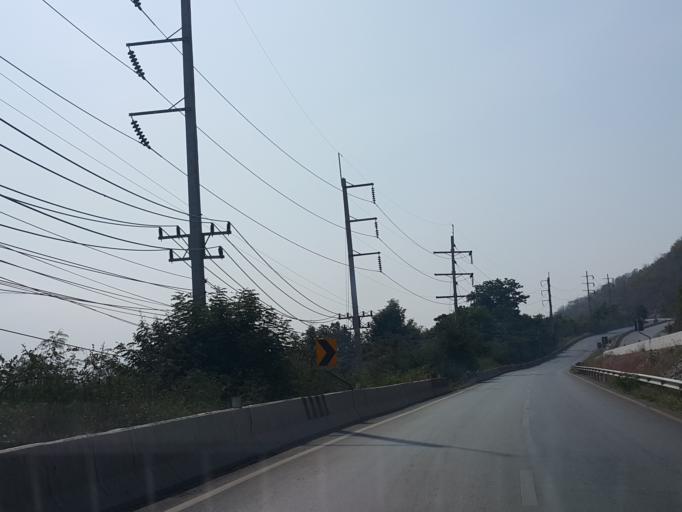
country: TH
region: Chiang Mai
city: Chom Thong
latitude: 18.3814
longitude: 98.6799
